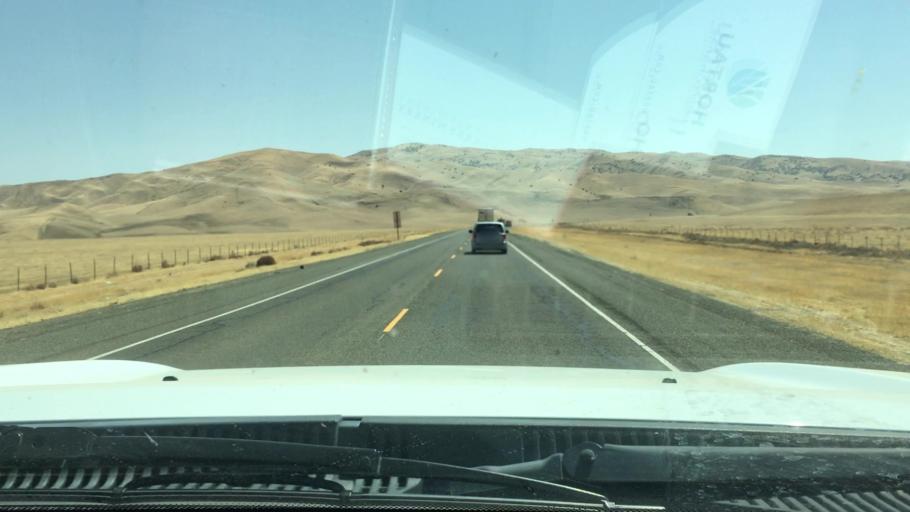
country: US
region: California
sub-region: Kings County
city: Avenal
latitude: 35.7957
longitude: -120.1074
